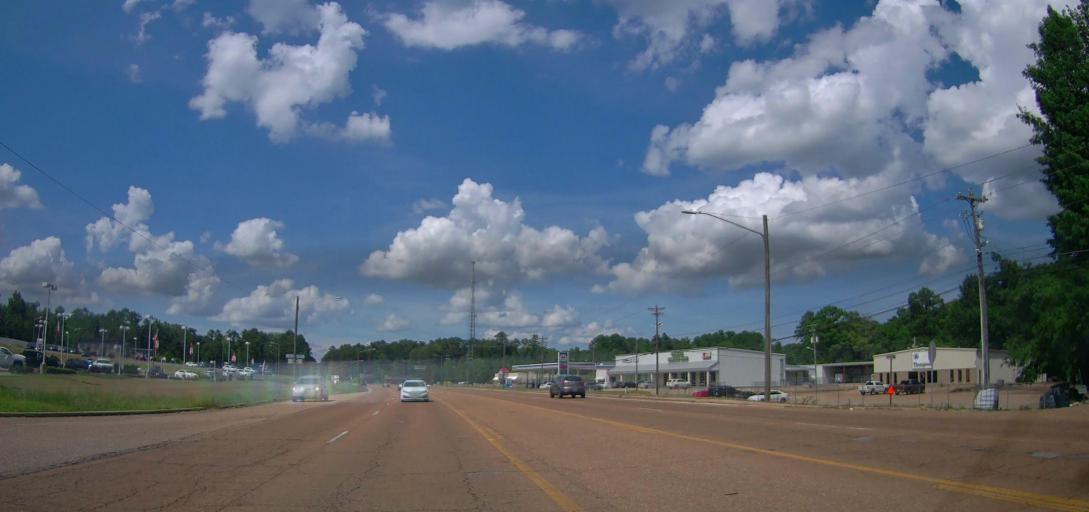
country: US
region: Mississippi
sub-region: Lowndes County
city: Columbus
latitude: 33.5488
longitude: -88.4336
